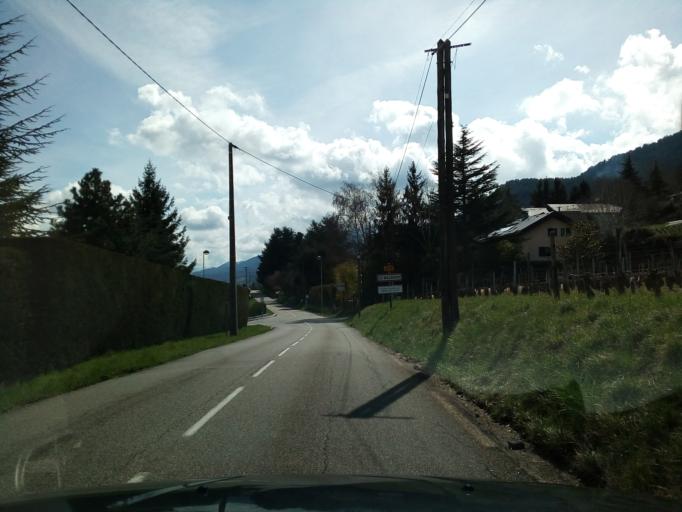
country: FR
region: Rhone-Alpes
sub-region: Departement de la Savoie
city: Saint-Baldoph
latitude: 45.5416
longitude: 5.9476
